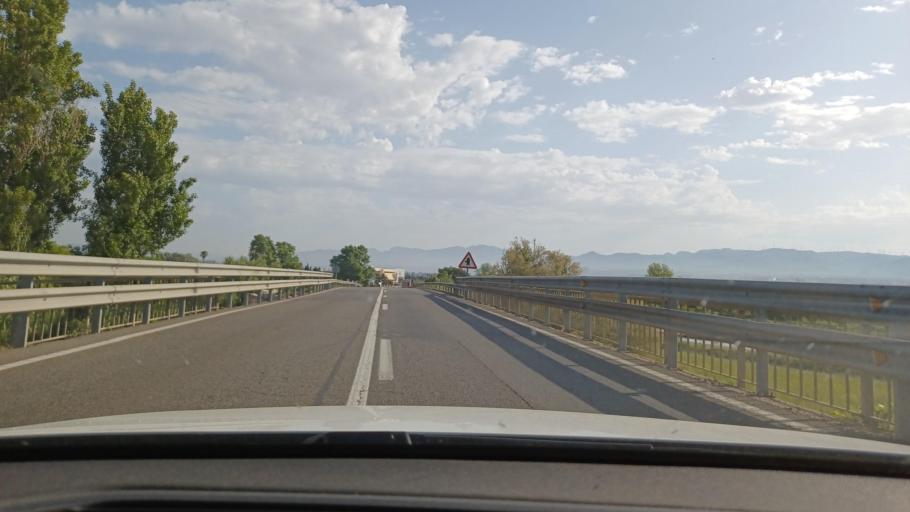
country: ES
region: Catalonia
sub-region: Provincia de Tarragona
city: Tortosa
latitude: 40.7915
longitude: 0.4963
